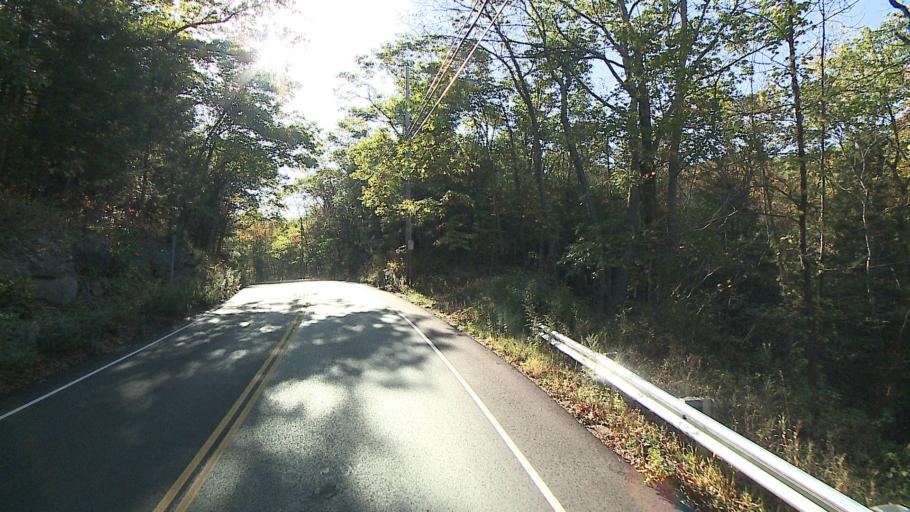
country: US
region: Connecticut
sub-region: Fairfield County
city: Georgetown
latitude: 41.3091
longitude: -73.4109
